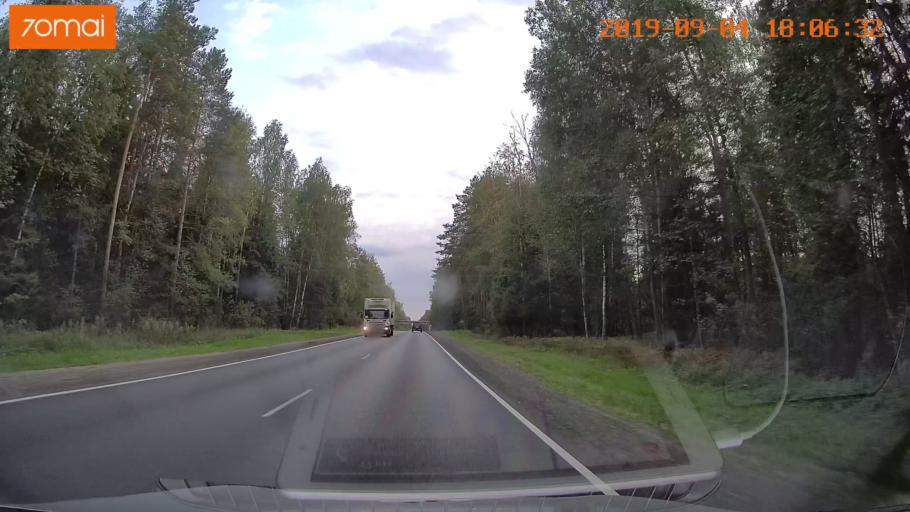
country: RU
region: Moskovskaya
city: Khorlovo
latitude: 55.4302
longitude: 38.8137
